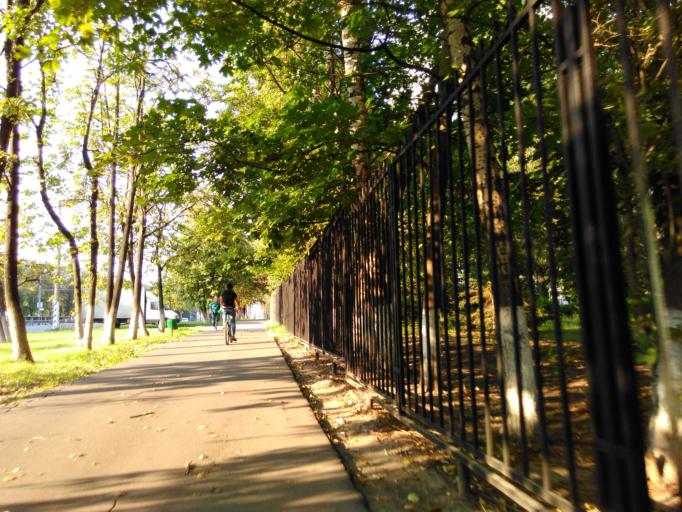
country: RU
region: Moskovskaya
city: Cheremushki
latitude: 55.6452
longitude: 37.5286
